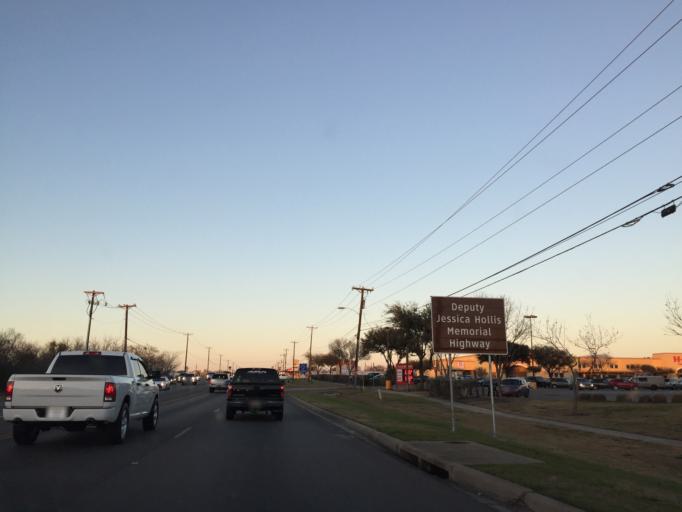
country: US
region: Texas
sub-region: Travis County
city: Pflugerville
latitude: 30.4368
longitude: -97.6137
